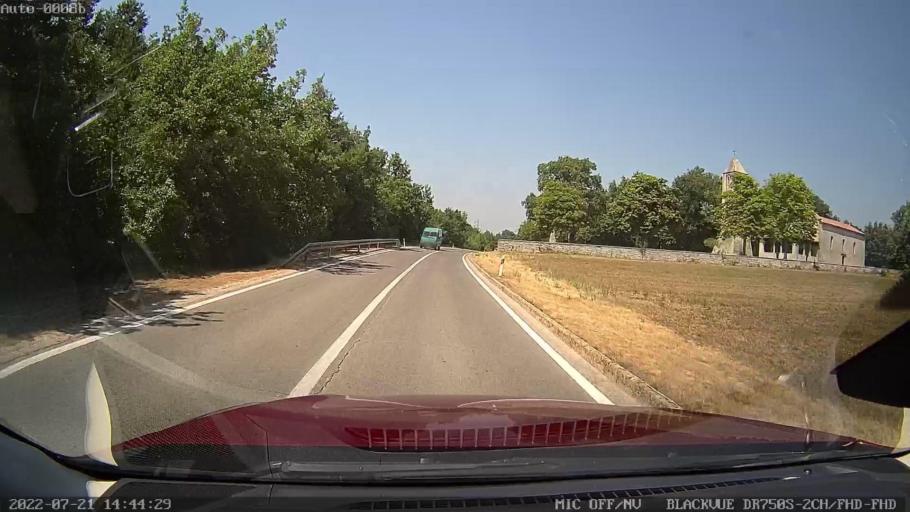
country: HR
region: Istarska
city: Pazin
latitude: 45.1181
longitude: 13.8844
